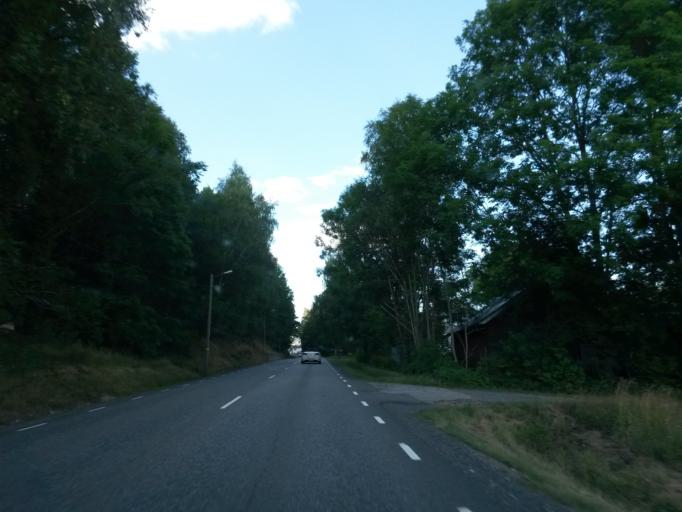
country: SE
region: Vaestra Goetaland
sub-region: Lerums Kommun
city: Grabo
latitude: 57.9219
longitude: 12.3548
